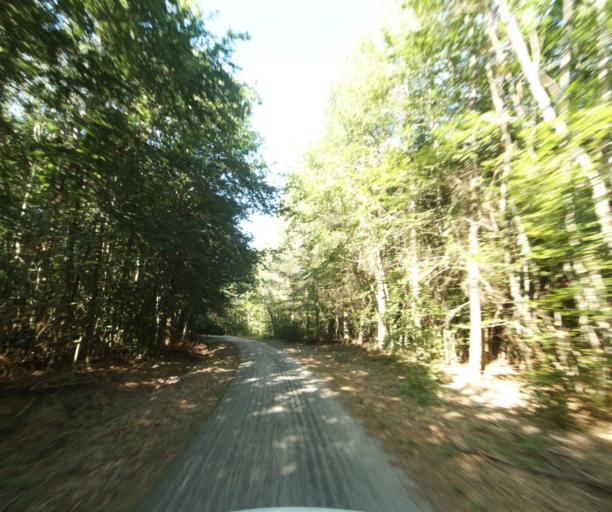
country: FR
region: Lorraine
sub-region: Departement des Vosges
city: Aydoilles
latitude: 48.1781
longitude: 6.5577
